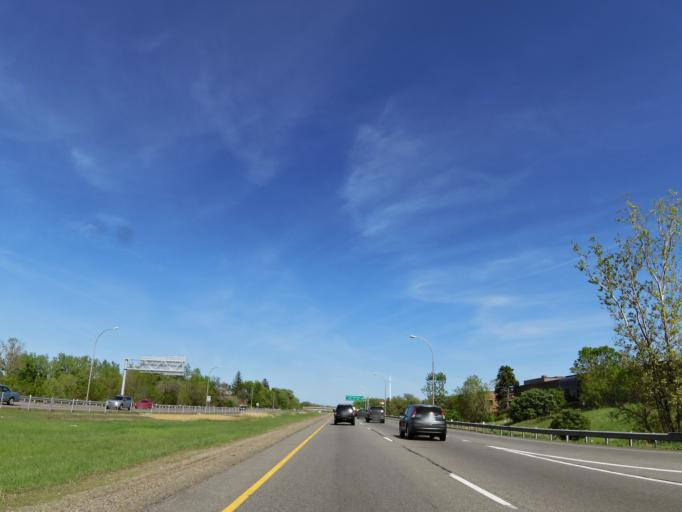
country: US
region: Minnesota
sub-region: Ramsey County
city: Roseville
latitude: 45.0101
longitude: -93.1636
